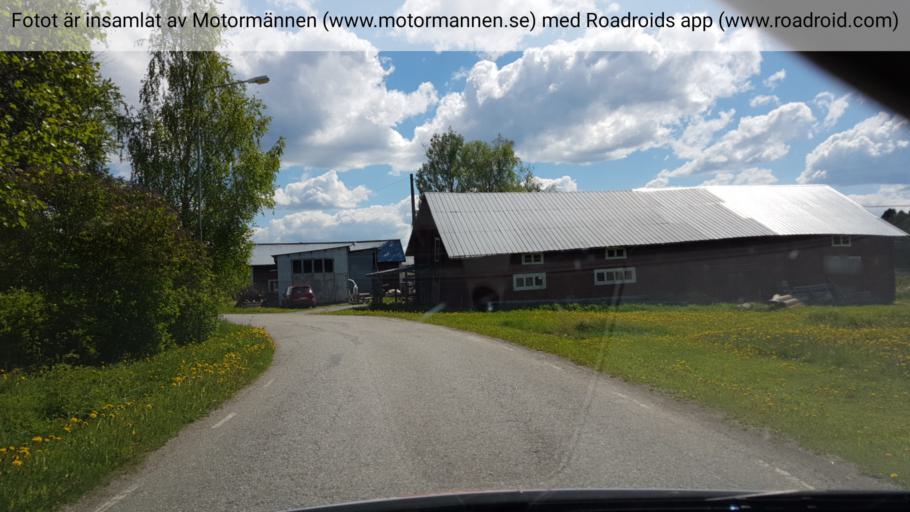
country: SE
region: Jaemtland
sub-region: Braecke Kommun
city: Braecke
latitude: 62.8297
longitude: 15.3130
